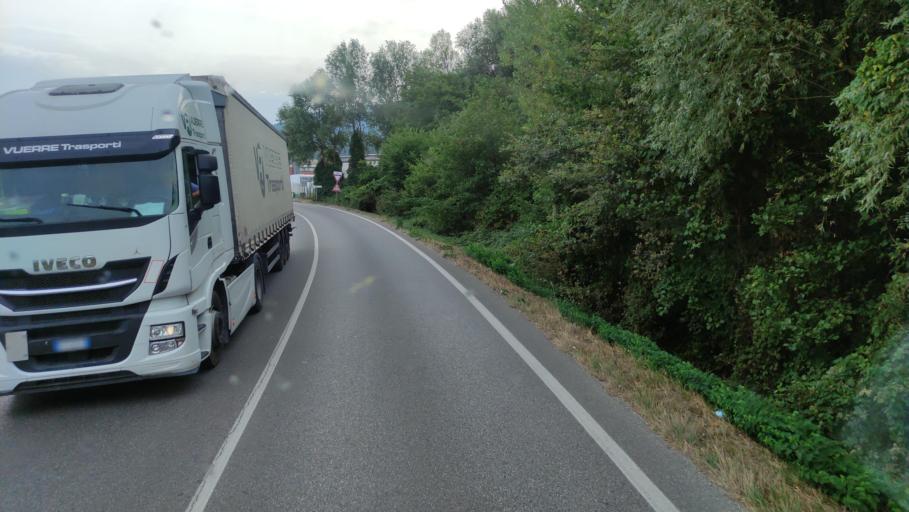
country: IT
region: Tuscany
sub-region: Provincia di Lucca
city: Lucca
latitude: 43.8164
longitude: 10.4948
